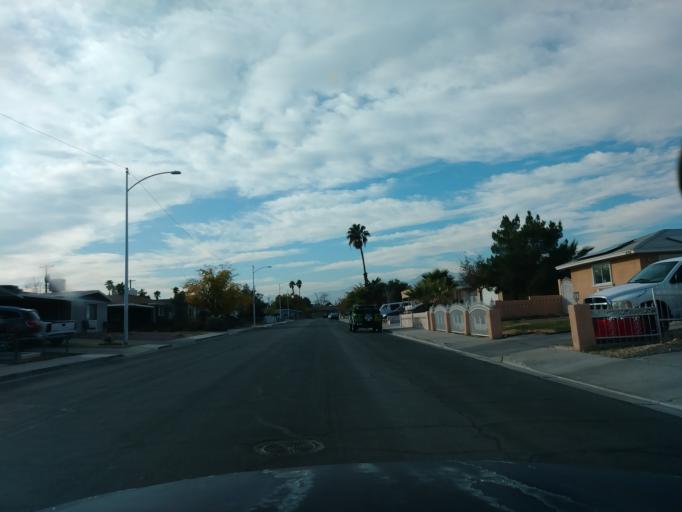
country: US
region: Nevada
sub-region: Clark County
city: Spring Valley
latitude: 36.1686
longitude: -115.2299
